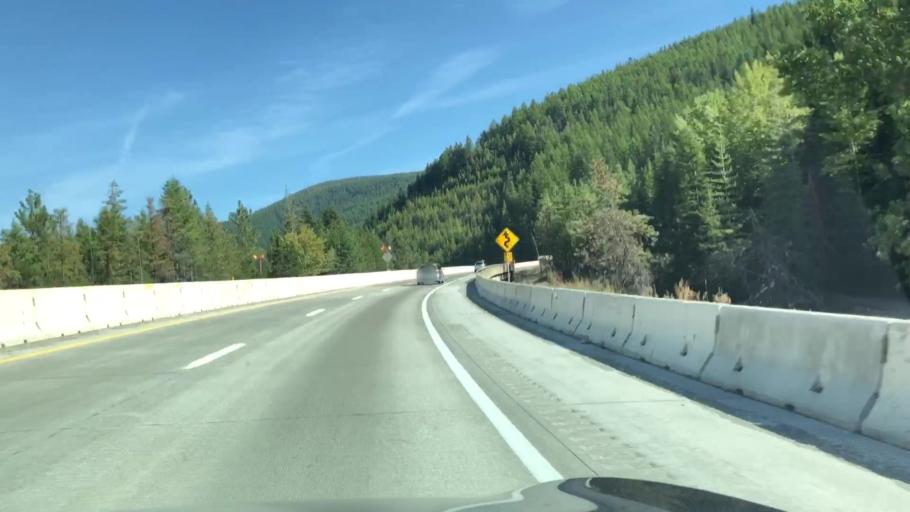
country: US
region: Idaho
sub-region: Shoshone County
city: Wallace
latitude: 47.4645
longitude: -115.7476
